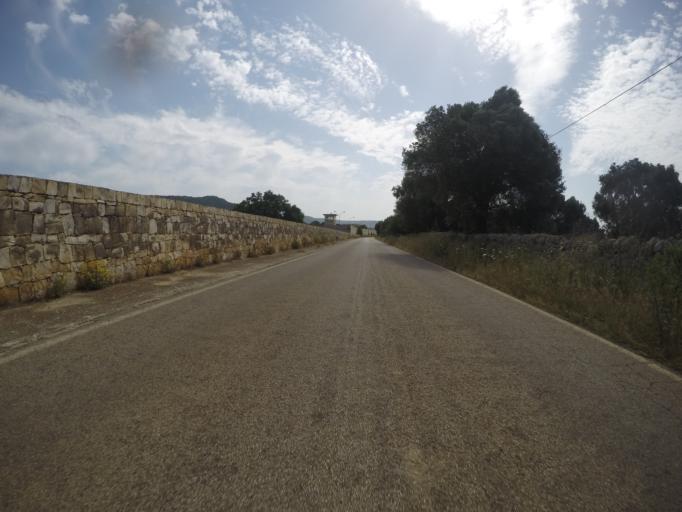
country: IT
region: Apulia
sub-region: Provincia di Taranto
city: Montemesola
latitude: 40.6141
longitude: 17.3502
